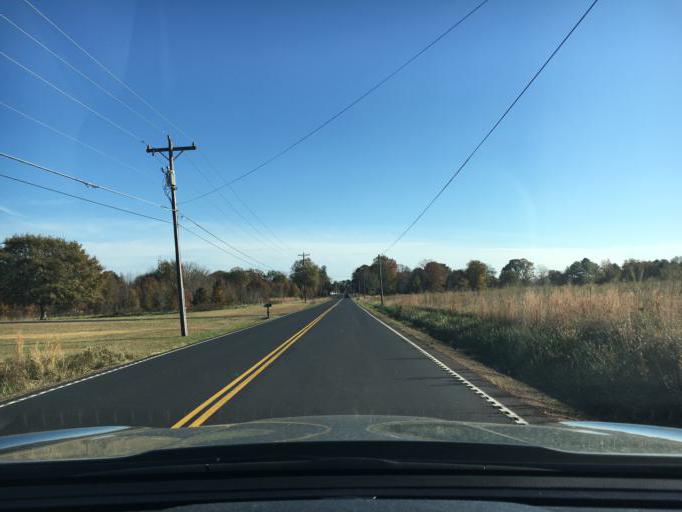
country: US
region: South Carolina
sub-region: Spartanburg County
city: Inman Mills
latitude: 35.0410
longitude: -82.1328
